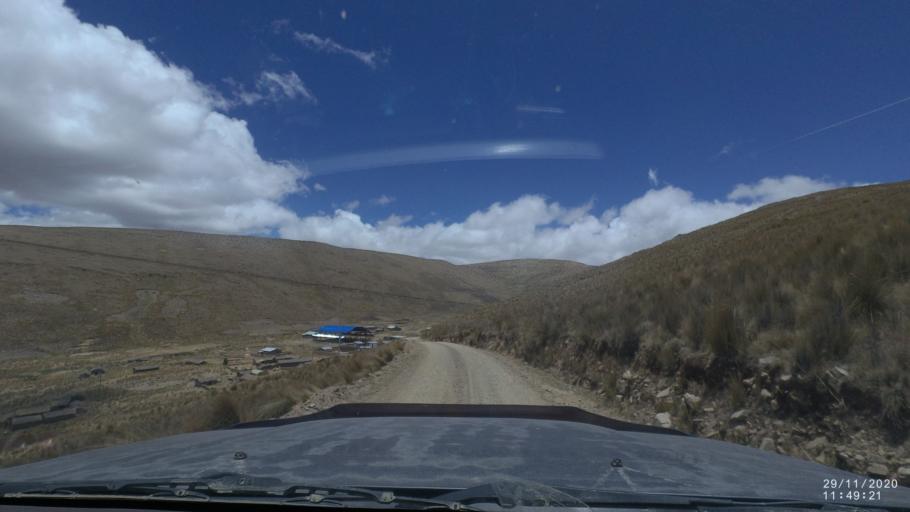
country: BO
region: Cochabamba
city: Cochabamba
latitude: -17.1764
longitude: -66.2599
